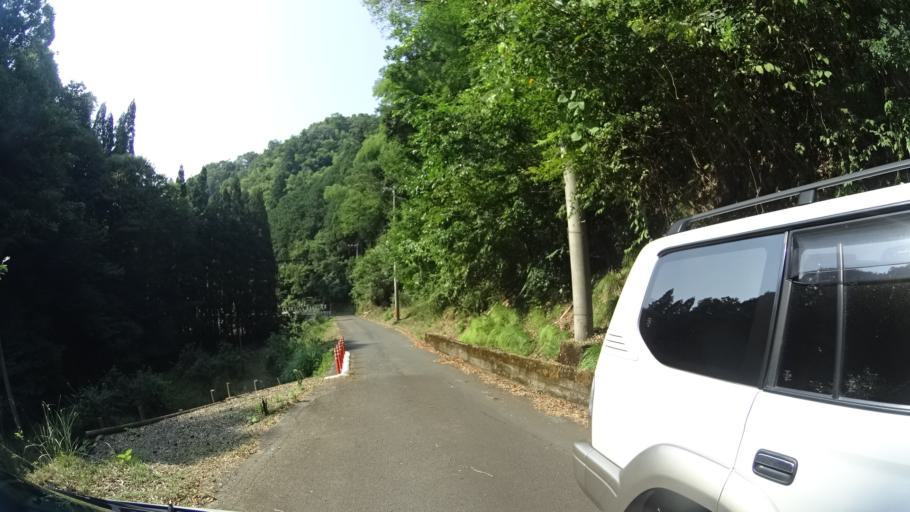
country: JP
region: Kyoto
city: Maizuru
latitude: 35.4079
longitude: 135.2342
